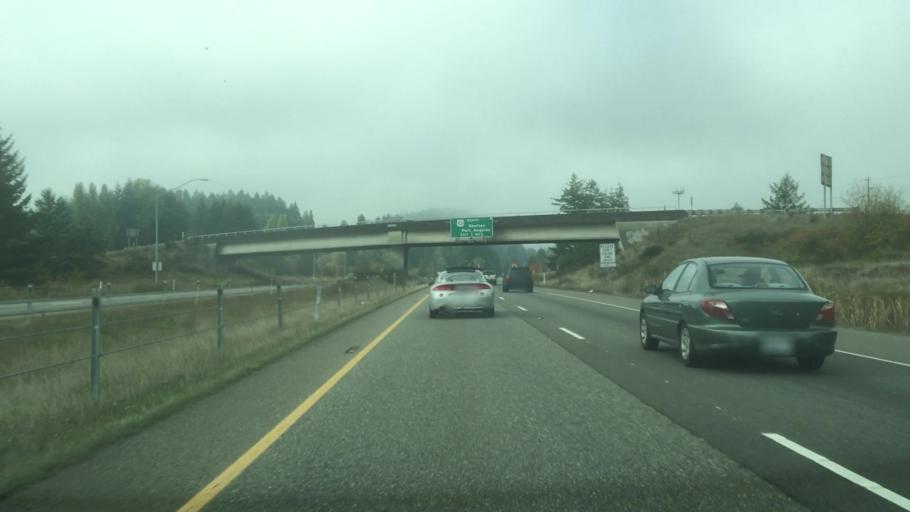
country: US
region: Washington
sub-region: Thurston County
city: Tumwater
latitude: 47.0466
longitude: -122.9935
